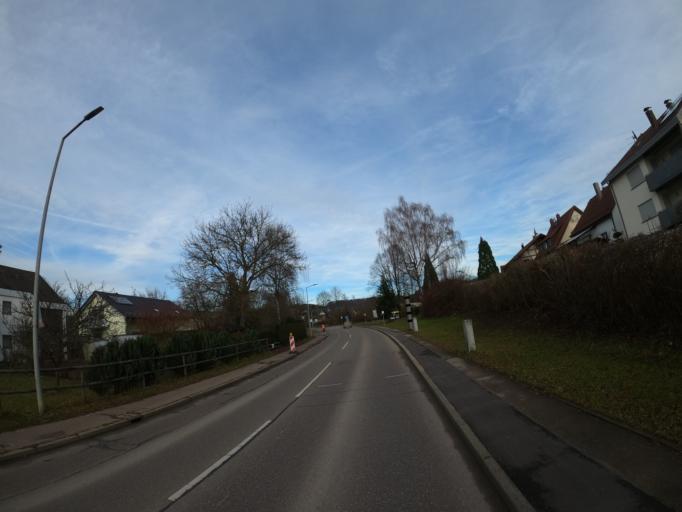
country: DE
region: Baden-Wuerttemberg
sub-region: Regierungsbezirk Stuttgart
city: Ottenbach
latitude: 48.7307
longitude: 9.7456
